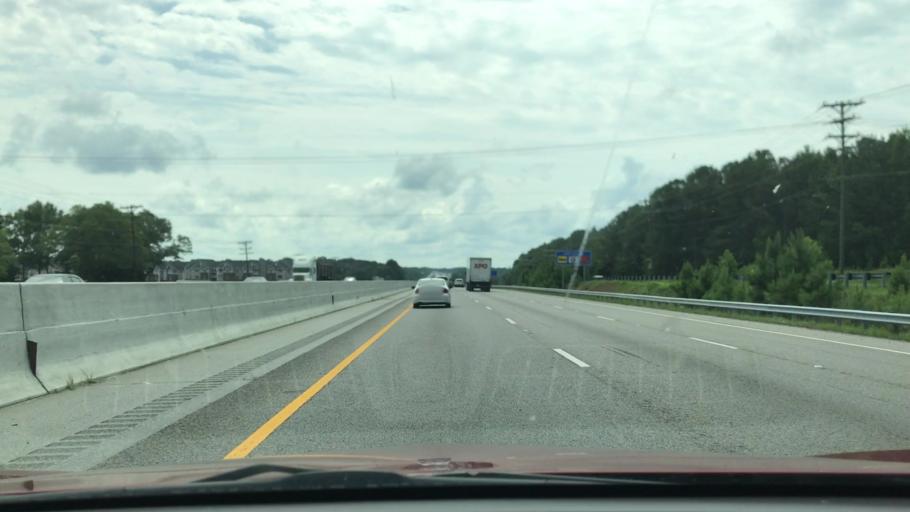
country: US
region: South Carolina
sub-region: Greenville County
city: Fountain Inn
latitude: 34.6860
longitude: -82.2139
